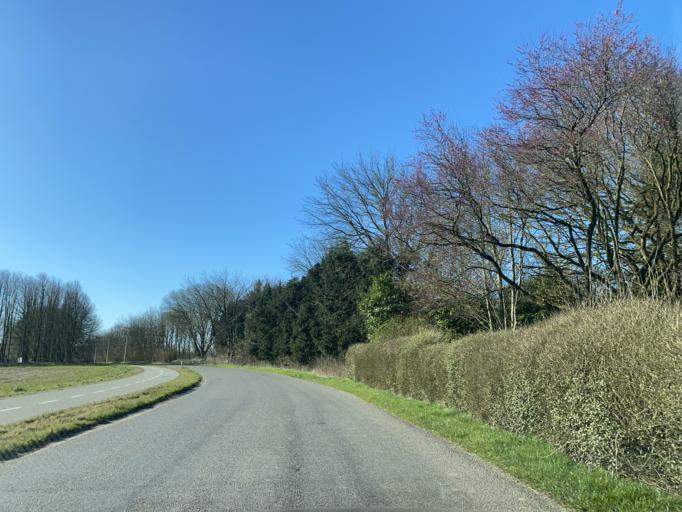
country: DK
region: Central Jutland
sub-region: Skanderborg Kommune
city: Skovby
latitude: 56.1927
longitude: 9.9637
